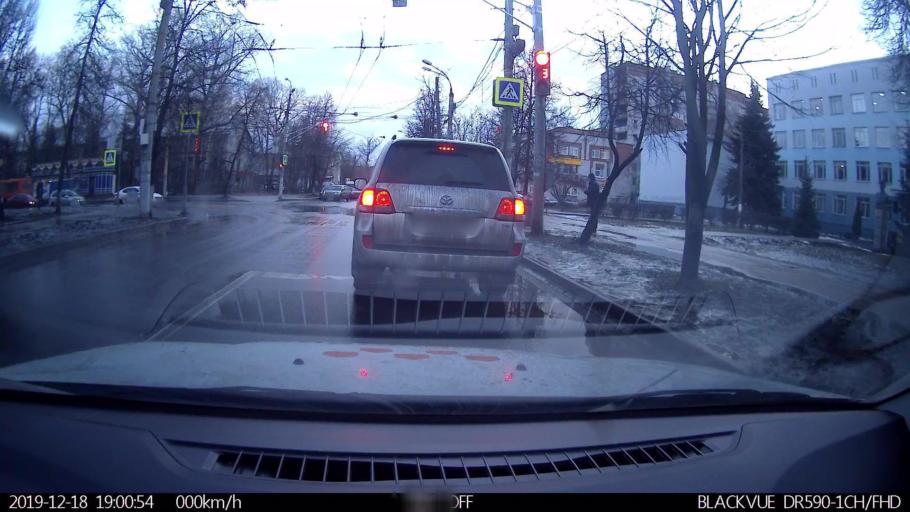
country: RU
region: Nizjnij Novgorod
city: Gorbatovka
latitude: 56.3290
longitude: 43.8526
